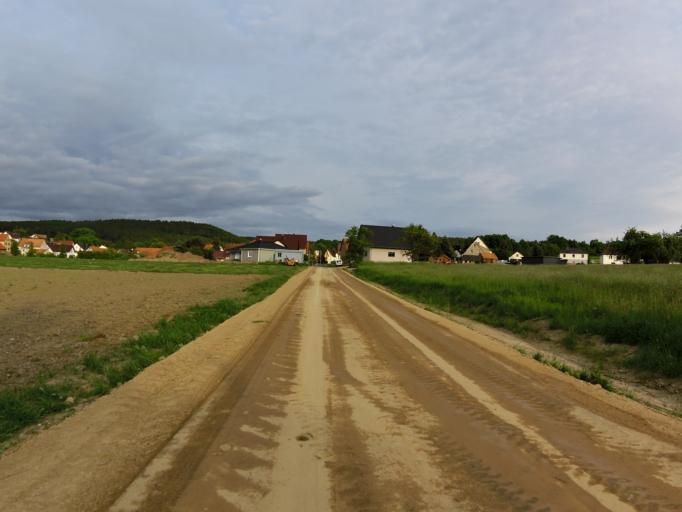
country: DE
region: Thuringia
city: Frauensee
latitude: 50.9090
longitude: 10.0960
